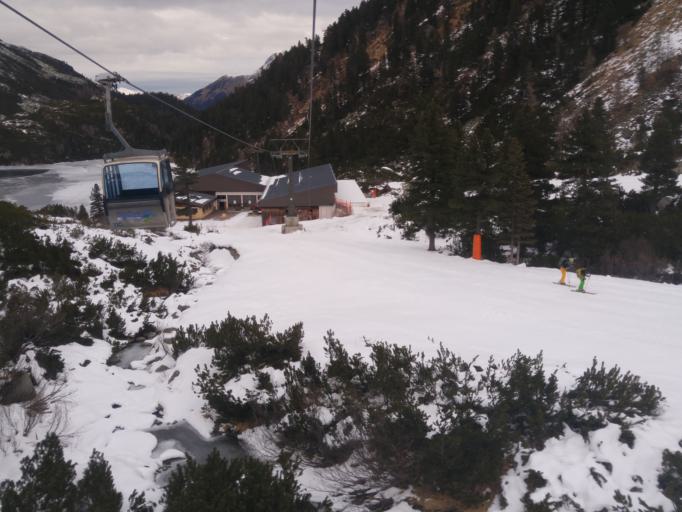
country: AT
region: Salzburg
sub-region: Politischer Bezirk Zell am See
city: Niedernsill
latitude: 47.1555
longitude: 12.6240
